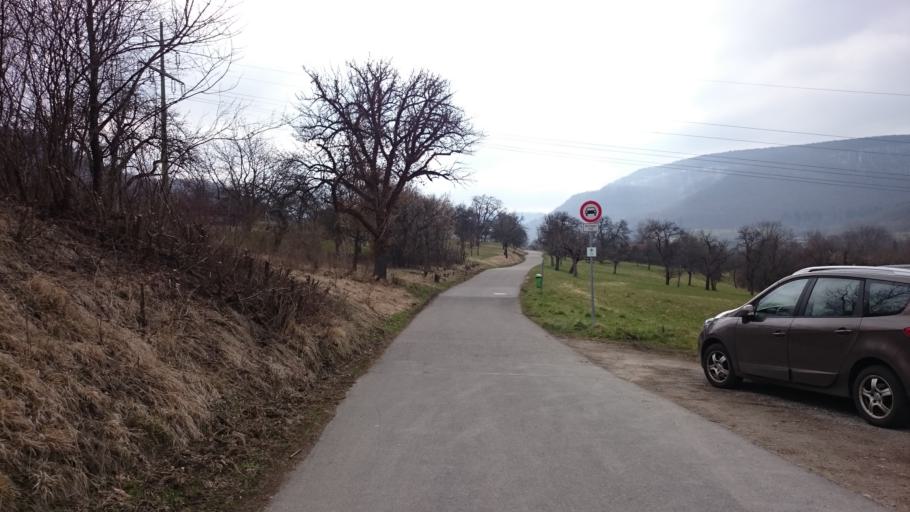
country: DE
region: Baden-Wuerttemberg
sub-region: Tuebingen Region
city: Pfullingen
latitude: 48.4564
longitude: 9.2355
